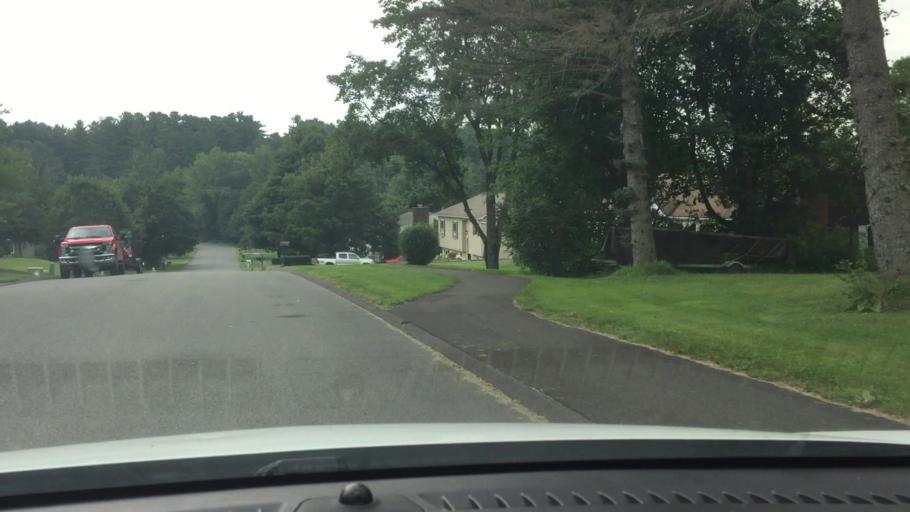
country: US
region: Massachusetts
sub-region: Berkshire County
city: Pittsfield
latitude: 42.4520
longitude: -73.2812
